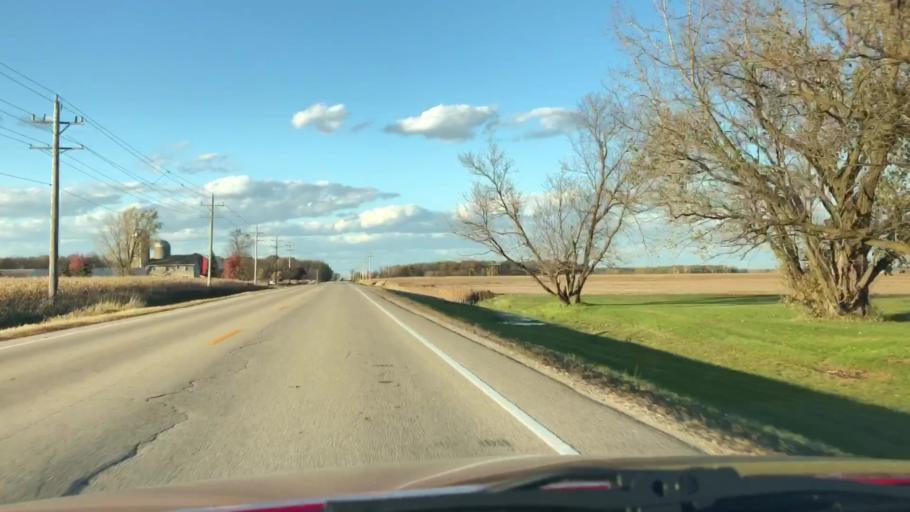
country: US
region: Wisconsin
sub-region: Outagamie County
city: Seymour
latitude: 44.4522
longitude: -88.2912
